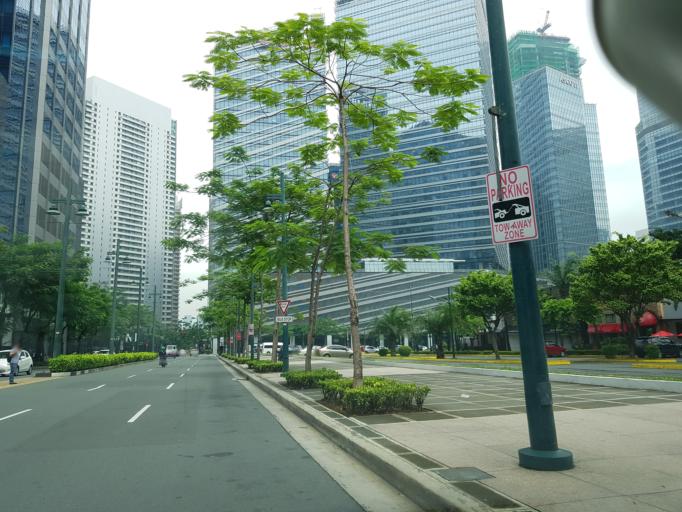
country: PH
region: Metro Manila
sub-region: Makati City
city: Makati City
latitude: 14.5485
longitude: 121.0484
